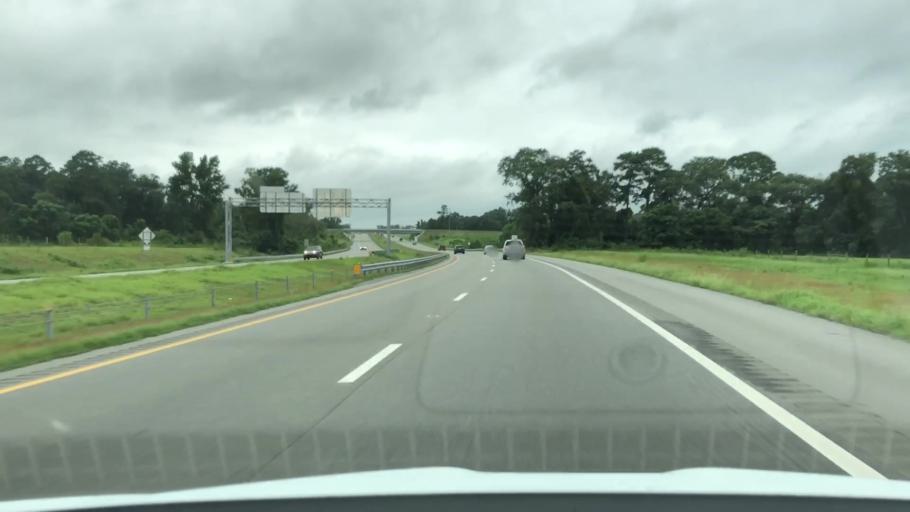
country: US
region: North Carolina
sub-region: Lenoir County
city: La Grange
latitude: 35.3077
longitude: -77.8212
